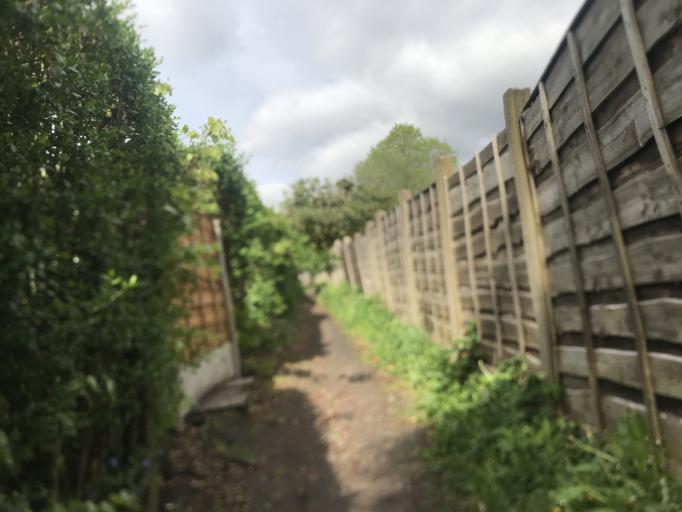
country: GB
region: England
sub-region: Borough of Stockport
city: Marple
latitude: 53.3969
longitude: -2.0576
